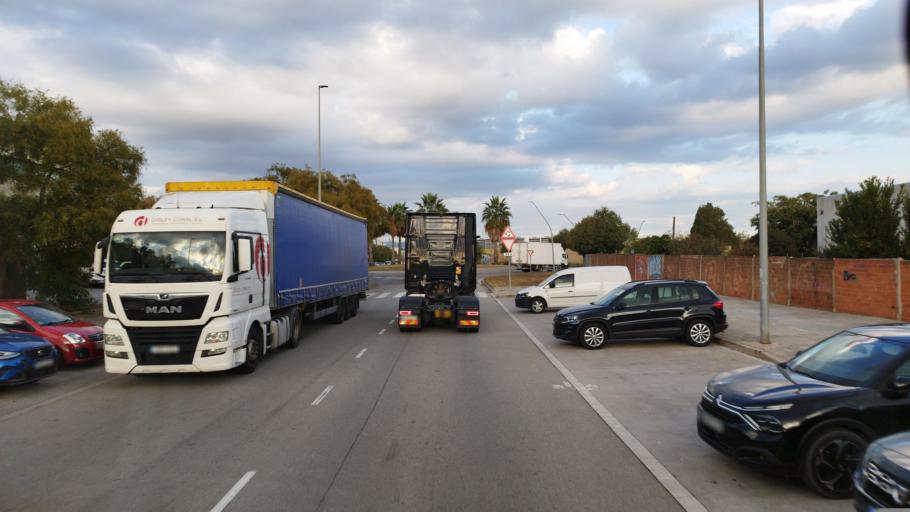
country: ES
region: Catalonia
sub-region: Provincia de Barcelona
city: Viladecans
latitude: 41.3027
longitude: 2.0151
